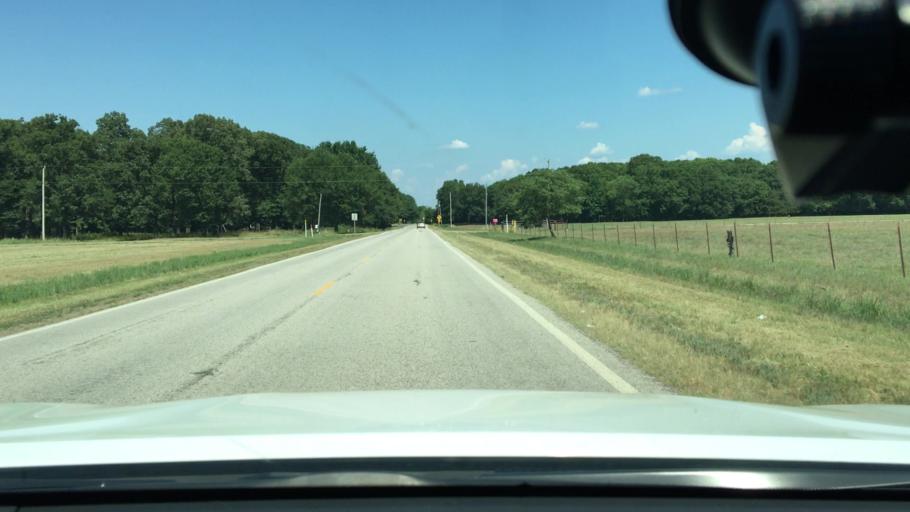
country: US
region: Arkansas
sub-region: Johnson County
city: Coal Hill
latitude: 35.3574
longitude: -93.5541
